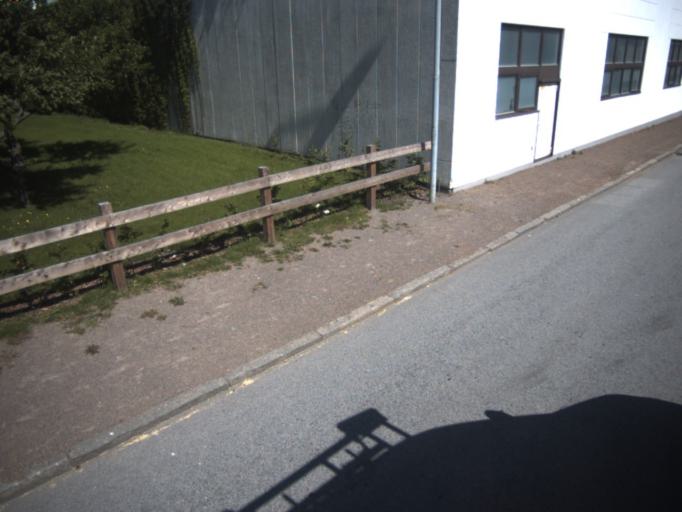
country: SE
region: Skane
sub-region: Helsingborg
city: Helsingborg
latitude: 56.0648
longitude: 12.7098
